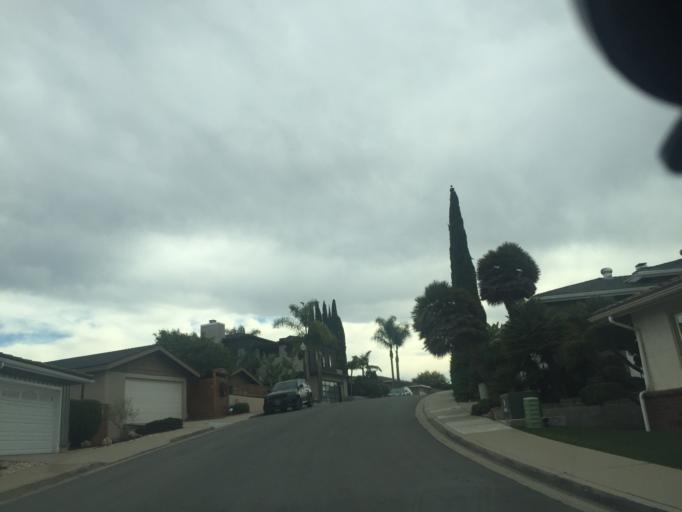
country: US
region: California
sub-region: San Diego County
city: Lemon Grove
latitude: 32.7693
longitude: -117.0937
